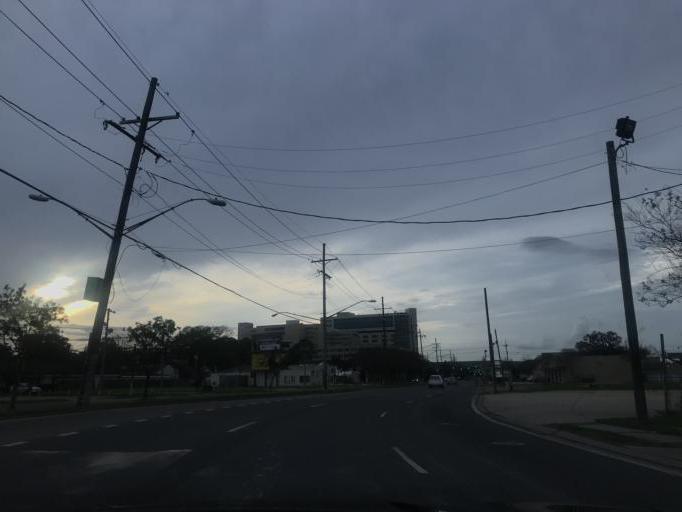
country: US
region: Louisiana
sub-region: Jefferson Parish
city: Jefferson
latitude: 29.9623
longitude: -90.1407
